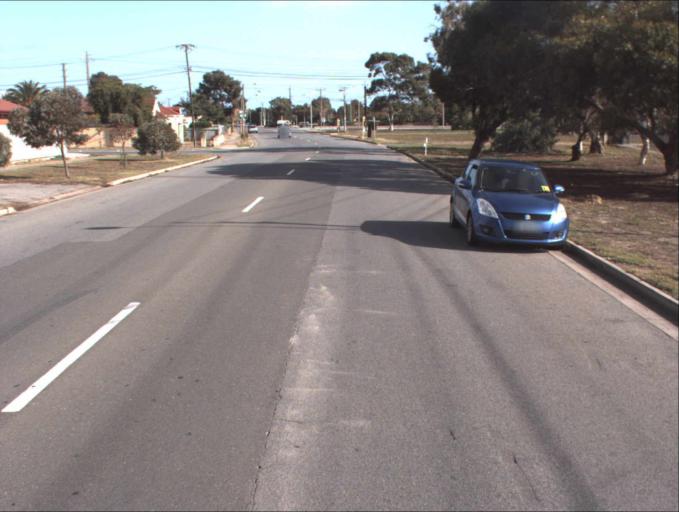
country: AU
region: South Australia
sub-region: Port Adelaide Enfield
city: Cheltenham
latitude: -34.8576
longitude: 138.5047
